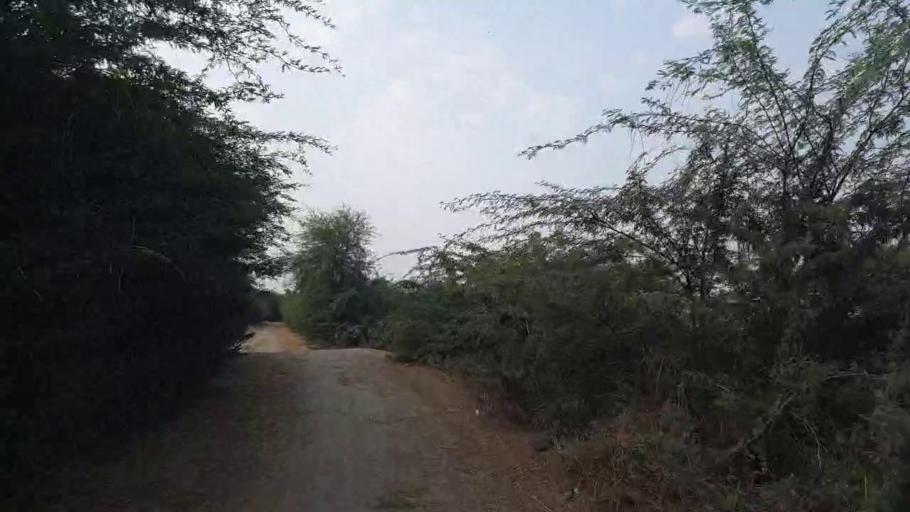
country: PK
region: Sindh
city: Talhar
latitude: 24.8455
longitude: 68.8128
